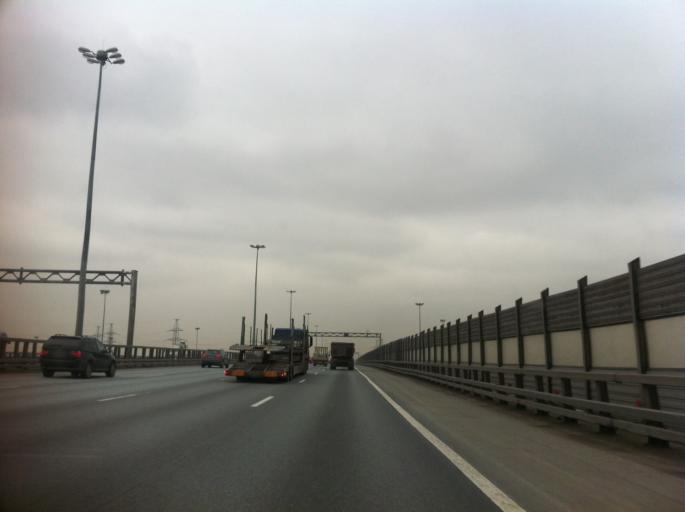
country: RU
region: St.-Petersburg
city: Obukhovo
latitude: 59.8325
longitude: 30.4446
